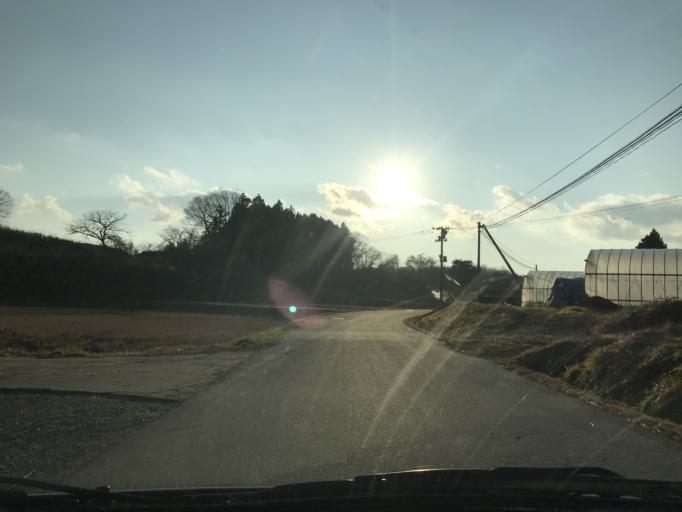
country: JP
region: Miyagi
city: Wakuya
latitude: 38.6975
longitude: 141.1099
